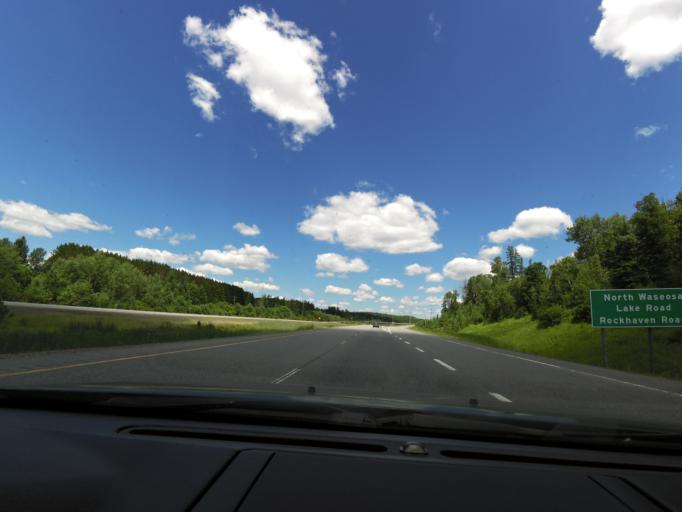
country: CA
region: Ontario
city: Huntsville
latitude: 45.4052
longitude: -79.2391
